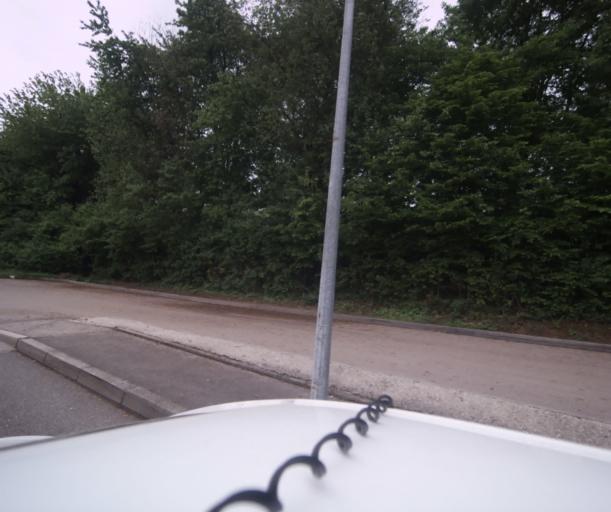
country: FR
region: Franche-Comte
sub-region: Departement du Doubs
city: Franois
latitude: 47.2140
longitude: 5.9441
